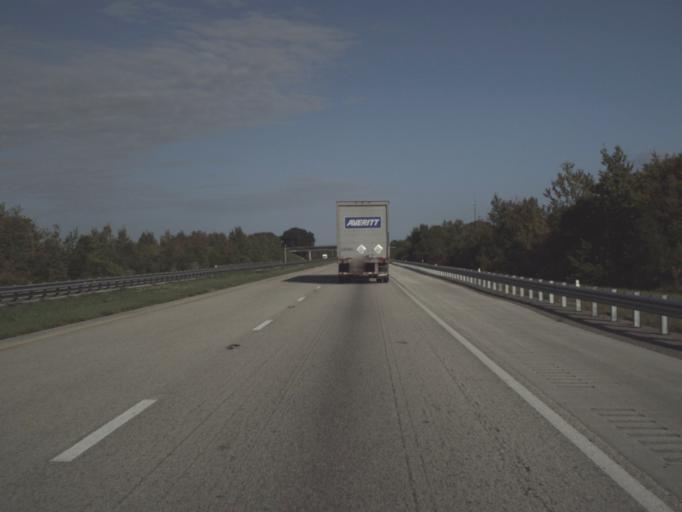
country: US
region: Florida
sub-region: Brevard County
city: June Park
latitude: 27.8732
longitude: -81.0206
